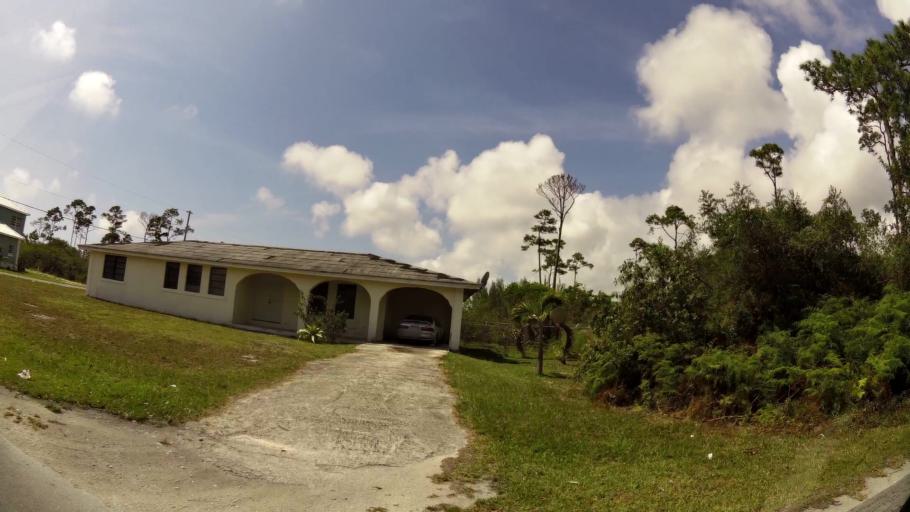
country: BS
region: Freeport
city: Freeport
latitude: 26.5107
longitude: -78.7249
